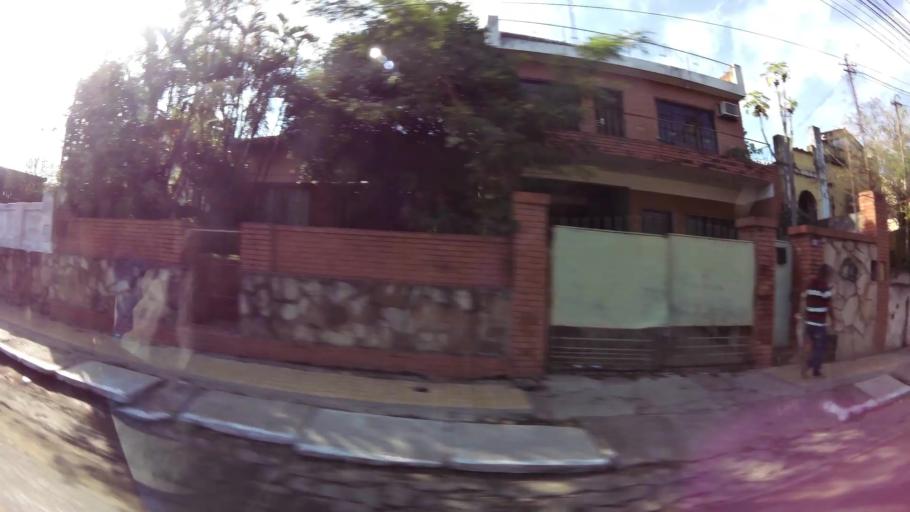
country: PY
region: Asuncion
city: Asuncion
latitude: -25.2765
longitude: -57.6111
